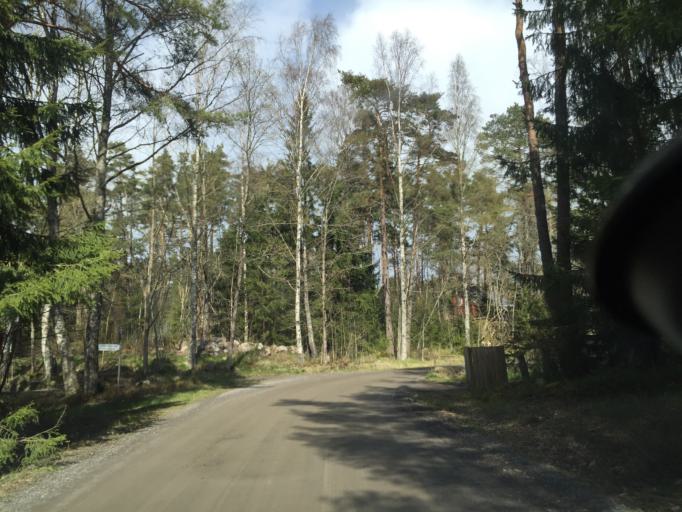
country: FI
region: Uusimaa
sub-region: Raaseporin
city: Hanko
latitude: 59.9426
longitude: 22.9158
